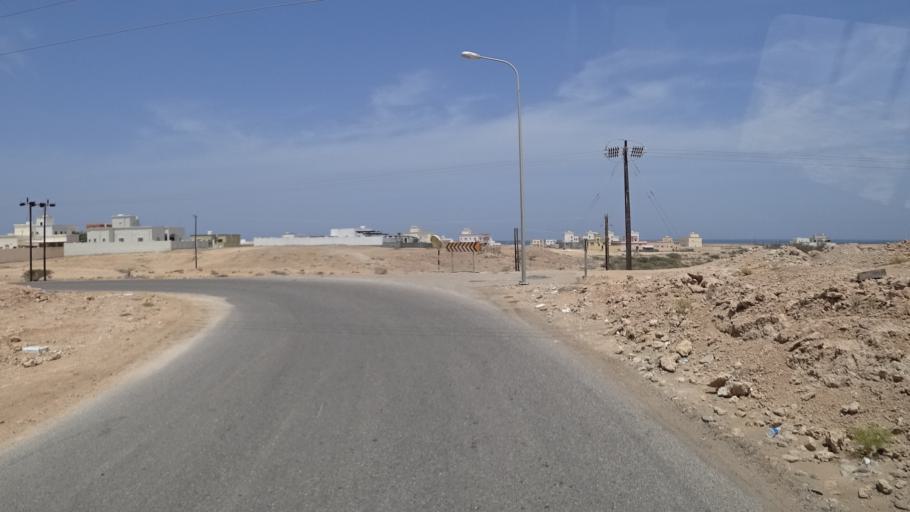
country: OM
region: Ash Sharqiyah
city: Sur
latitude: 22.6153
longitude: 59.4553
